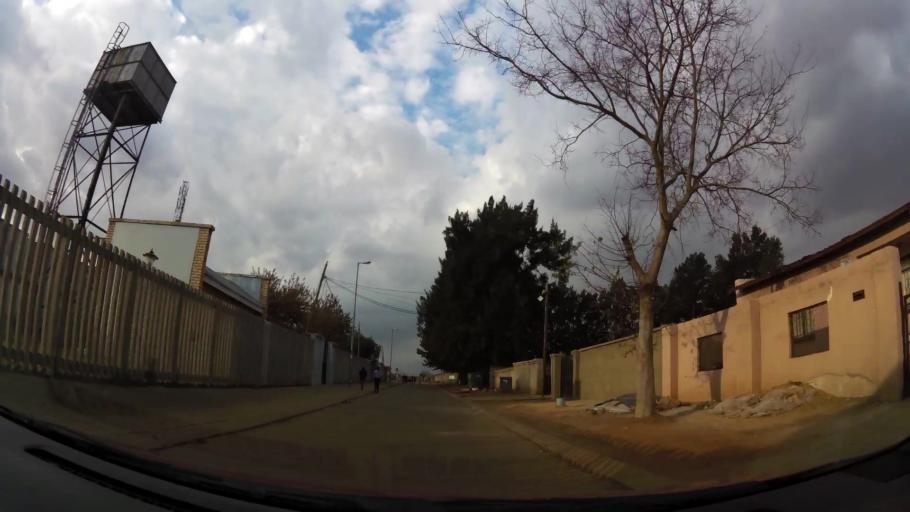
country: ZA
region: Gauteng
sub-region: City of Johannesburg Metropolitan Municipality
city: Soweto
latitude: -26.2395
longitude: 27.8237
